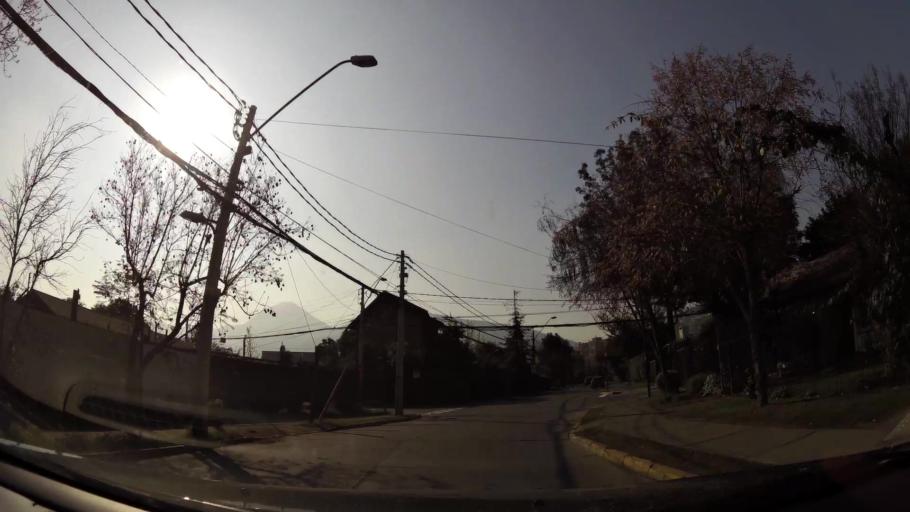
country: CL
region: Santiago Metropolitan
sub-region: Provincia de Santiago
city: Villa Presidente Frei, Nunoa, Santiago, Chile
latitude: -33.3808
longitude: -70.5449
